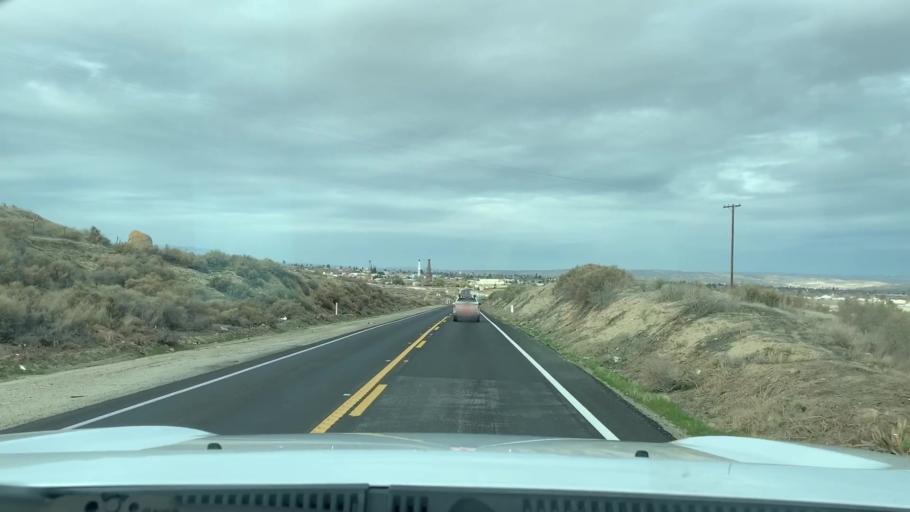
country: US
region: California
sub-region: Kern County
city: South Taft
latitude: 35.1265
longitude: -119.4406
